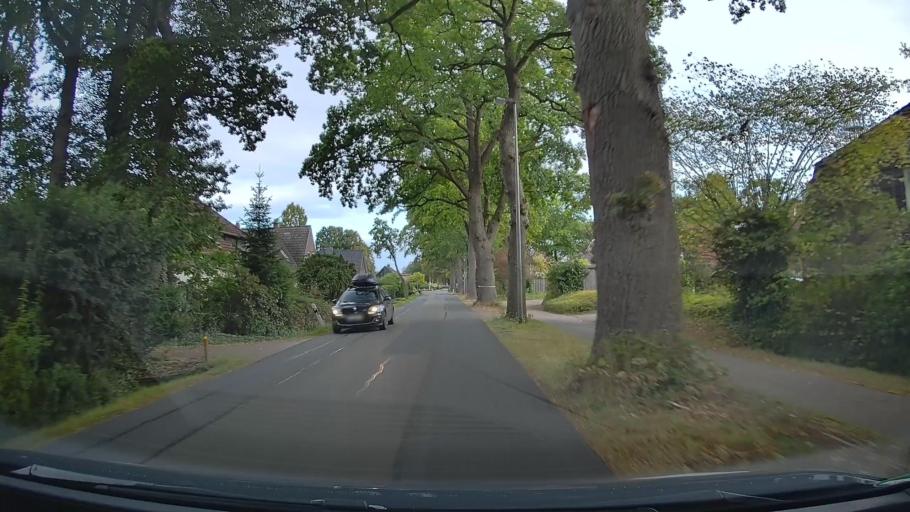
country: DE
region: Lower Saxony
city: Oldenburg
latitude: 53.1379
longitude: 8.1462
